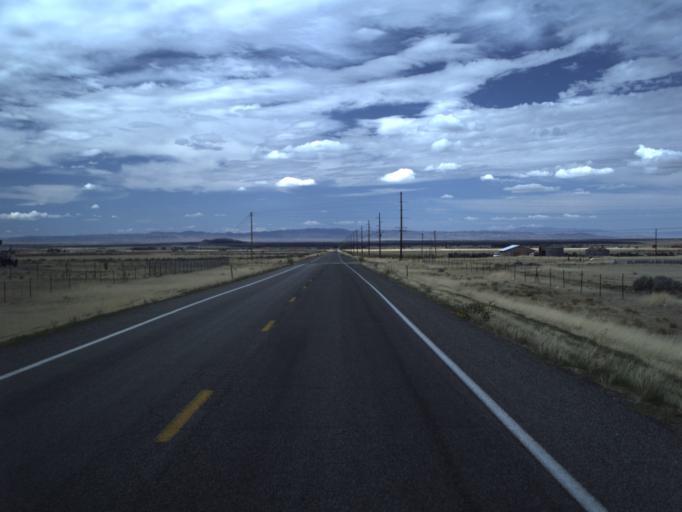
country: US
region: Utah
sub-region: Millard County
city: Fillmore
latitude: 38.9792
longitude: -112.3504
